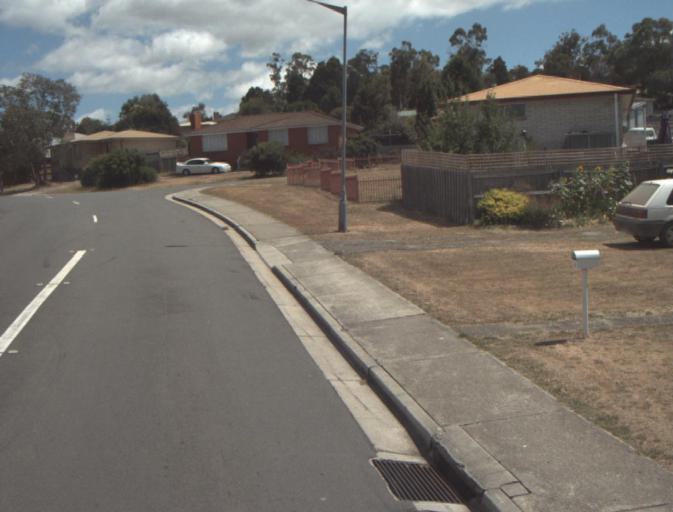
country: AU
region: Tasmania
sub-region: Launceston
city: Newstead
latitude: -41.4101
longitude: 147.1692
